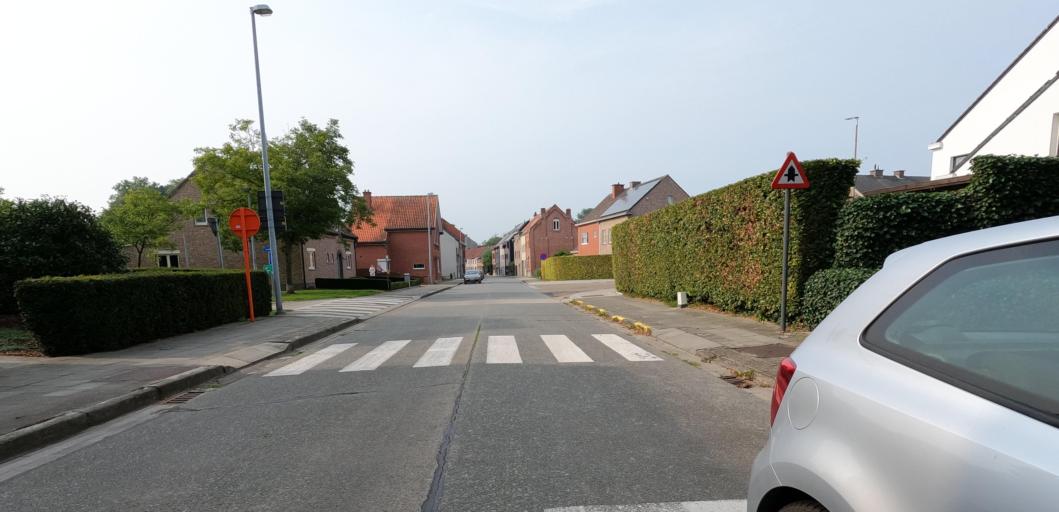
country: BE
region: Flanders
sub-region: Provincie Oost-Vlaanderen
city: Temse
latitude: 51.1266
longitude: 4.2266
